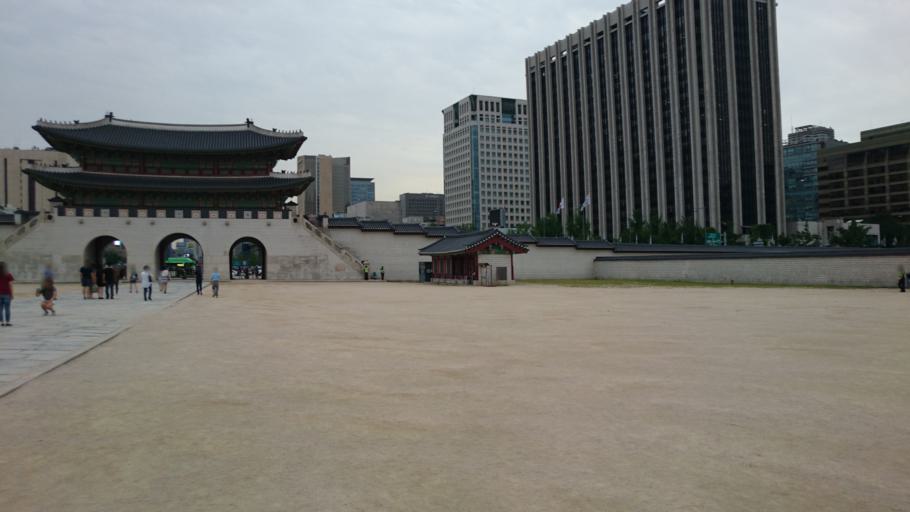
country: KR
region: Seoul
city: Seoul
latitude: 37.5768
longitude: 126.9768
